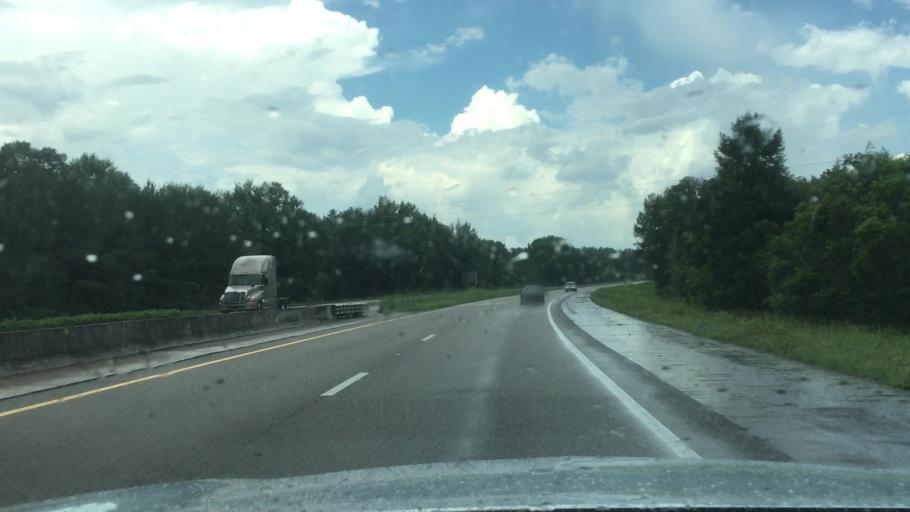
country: US
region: Mississippi
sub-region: Jones County
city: Laurel
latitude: 31.7043
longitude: -89.1168
